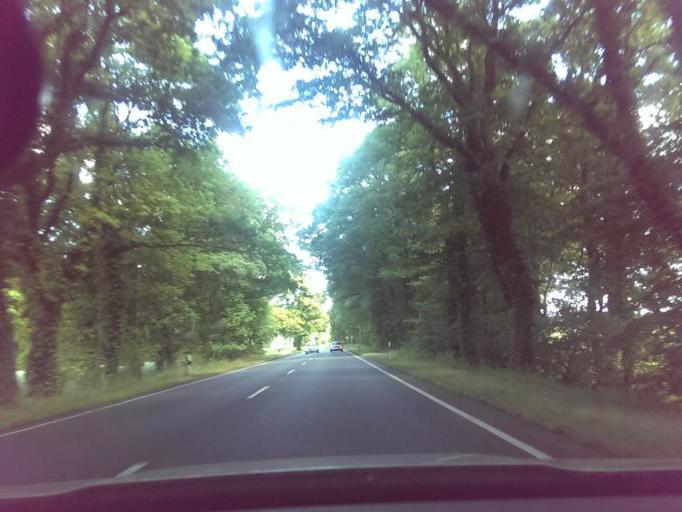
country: DE
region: Lower Saxony
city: Kirchlinteln
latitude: 53.0048
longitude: 9.2711
